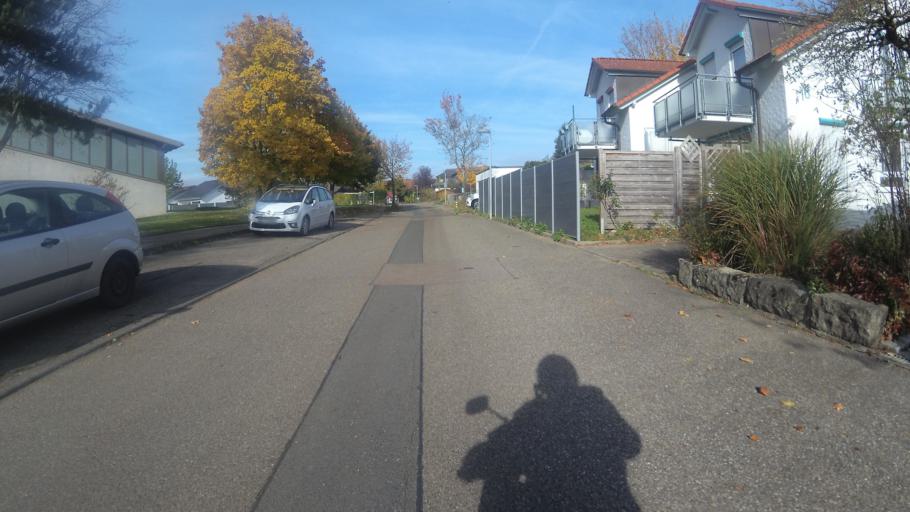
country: DE
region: Baden-Wuerttemberg
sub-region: Regierungsbezirk Stuttgart
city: Oedheim
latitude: 49.2418
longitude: 9.2460
